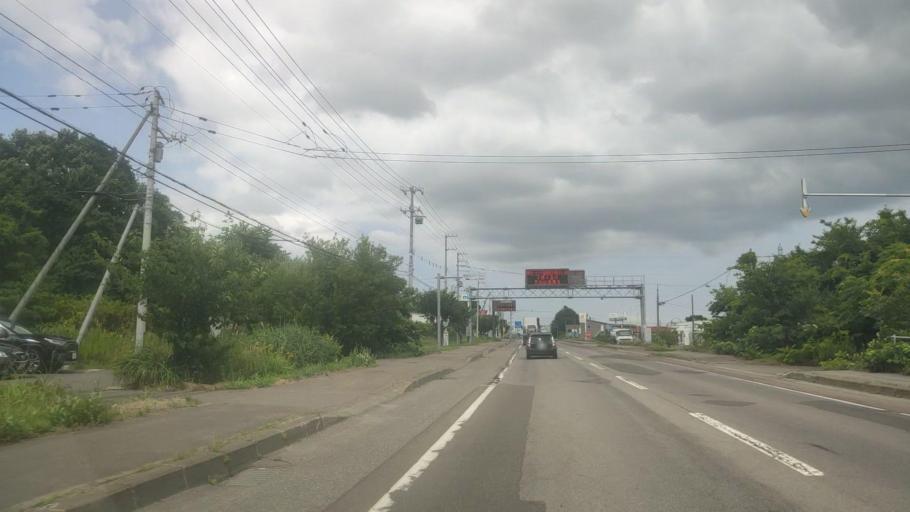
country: JP
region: Hokkaido
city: Nanae
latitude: 42.0905
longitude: 140.5800
